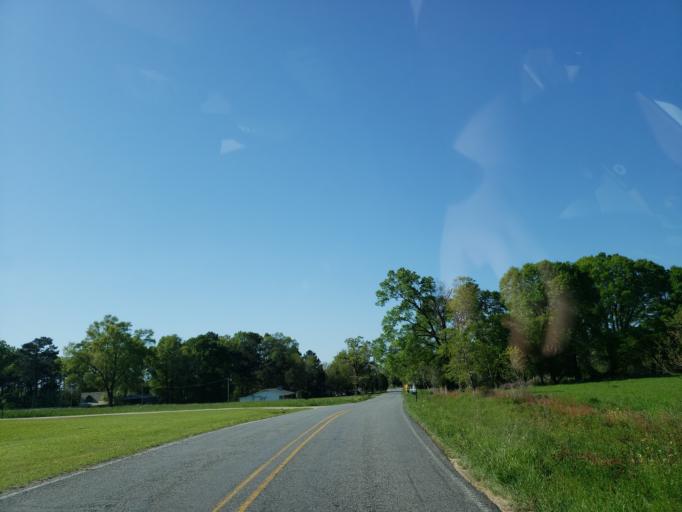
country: US
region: Mississippi
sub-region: Forrest County
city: Rawls Springs
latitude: 31.5377
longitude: -89.3635
